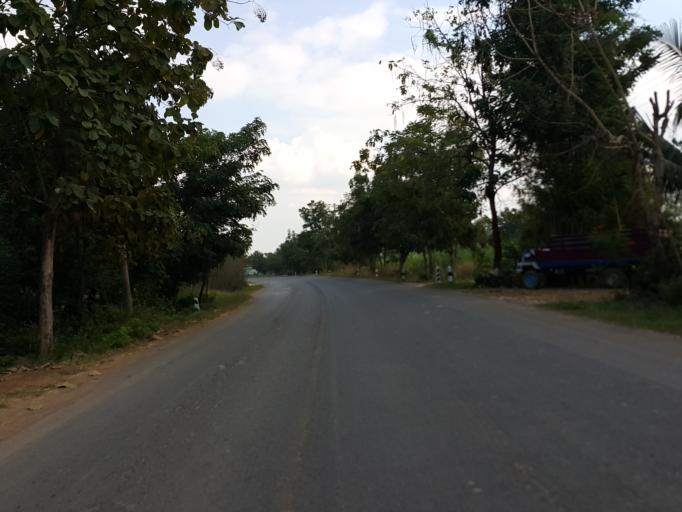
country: TH
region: Sukhothai
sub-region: Amphoe Si Satchanalai
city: Si Satchanalai
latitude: 17.4591
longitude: 99.6675
